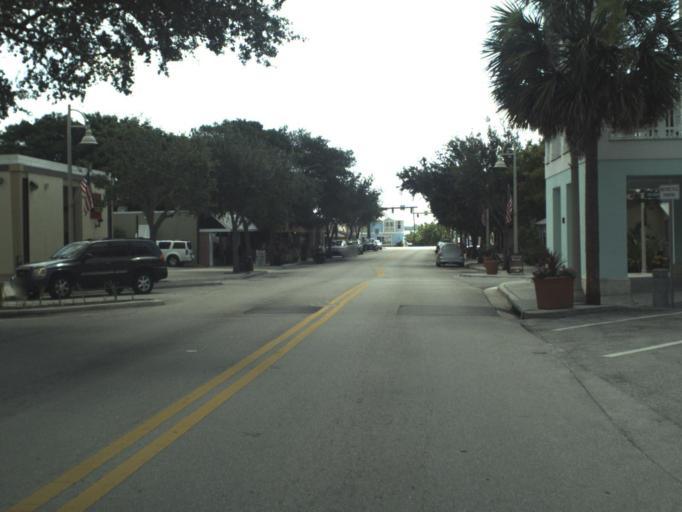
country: US
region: Florida
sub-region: Martin County
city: Jensen Beach
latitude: 27.2439
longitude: -80.2269
